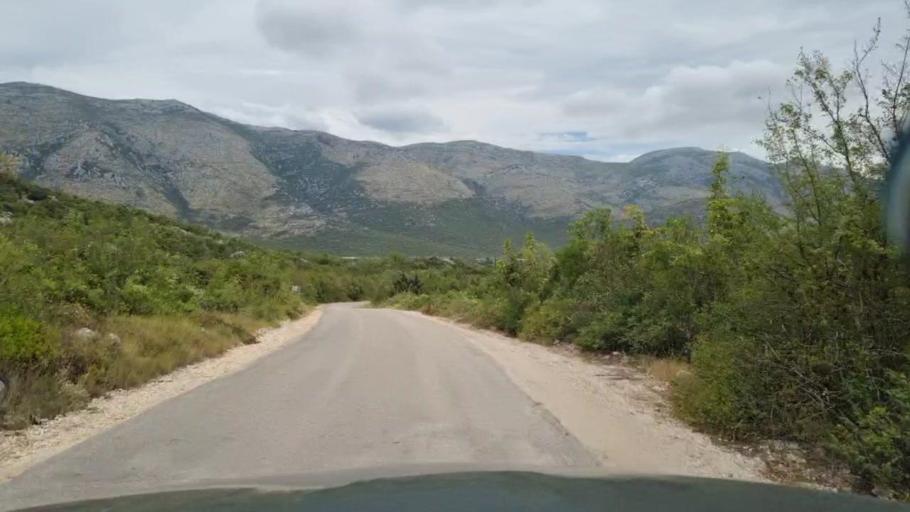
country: BA
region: Federation of Bosnia and Herzegovina
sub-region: Hercegovacko-Bosanski Kanton
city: Neum
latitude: 42.9472
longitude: 17.7023
